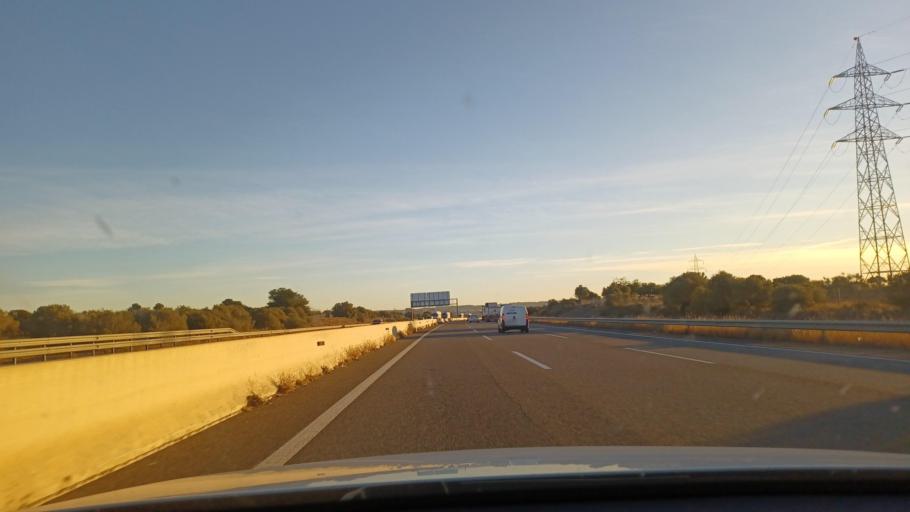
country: ES
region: Catalonia
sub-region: Provincia de Tarragona
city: Constanti
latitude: 41.1413
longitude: 1.1909
